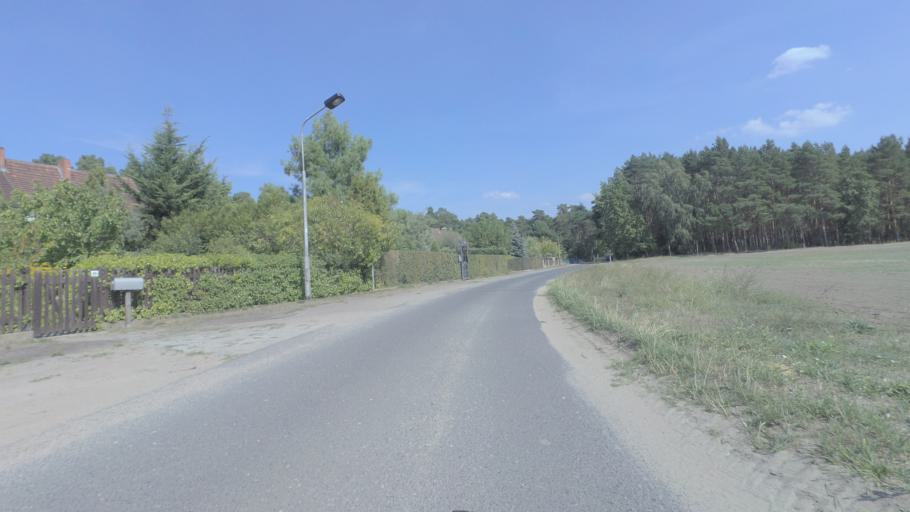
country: DE
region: Brandenburg
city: Am Mellensee
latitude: 52.1924
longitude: 13.3476
